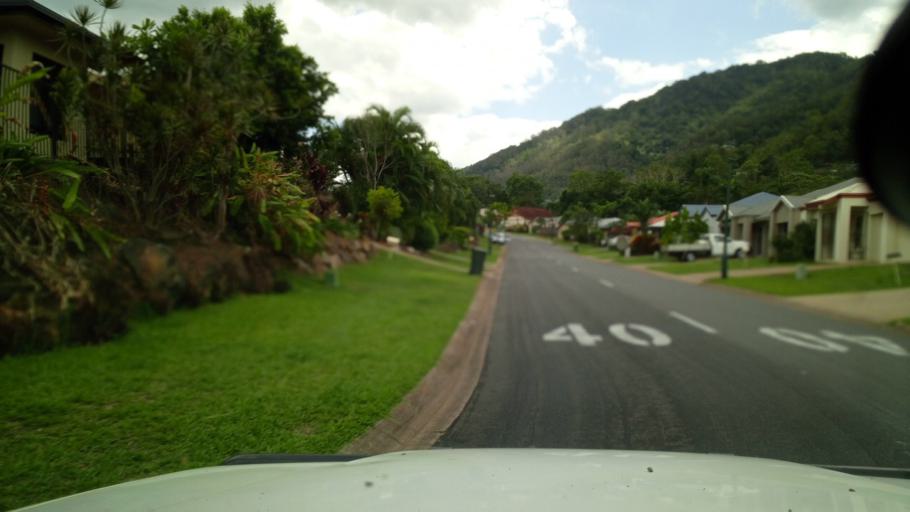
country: AU
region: Queensland
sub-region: Cairns
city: Redlynch
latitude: -16.9104
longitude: 145.7176
